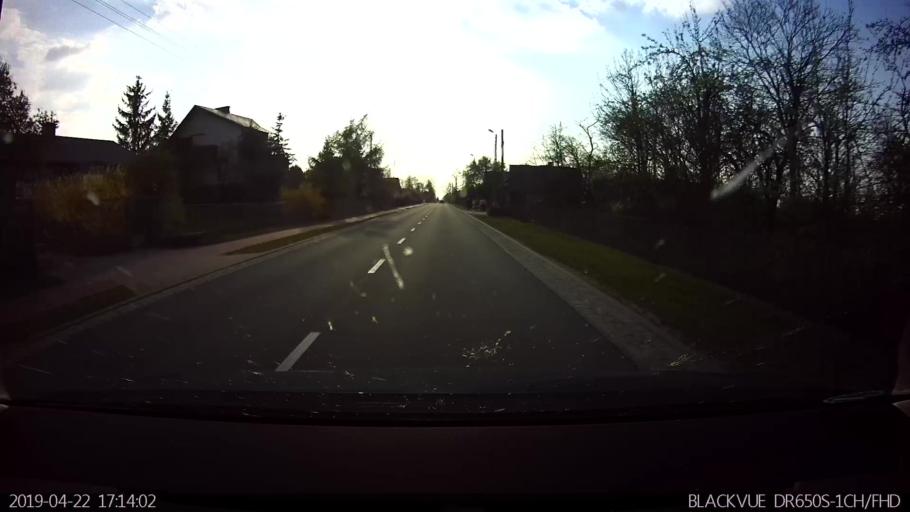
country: PL
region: Masovian Voivodeship
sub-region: Powiat sokolowski
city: Jablonna Lacka
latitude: 52.4012
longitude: 22.5089
